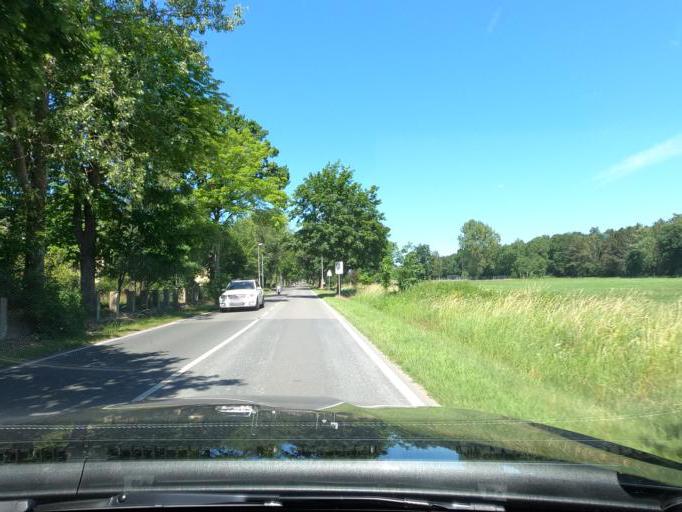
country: DE
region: Lower Saxony
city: Wathlingen
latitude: 52.5236
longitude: 10.1404
